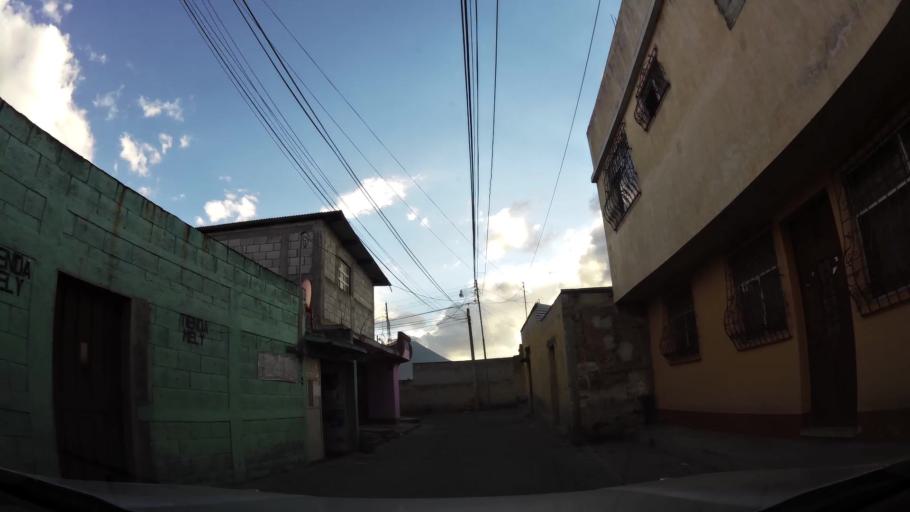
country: GT
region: Quetzaltenango
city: Quetzaltenango
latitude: 14.8527
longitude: -91.5303
